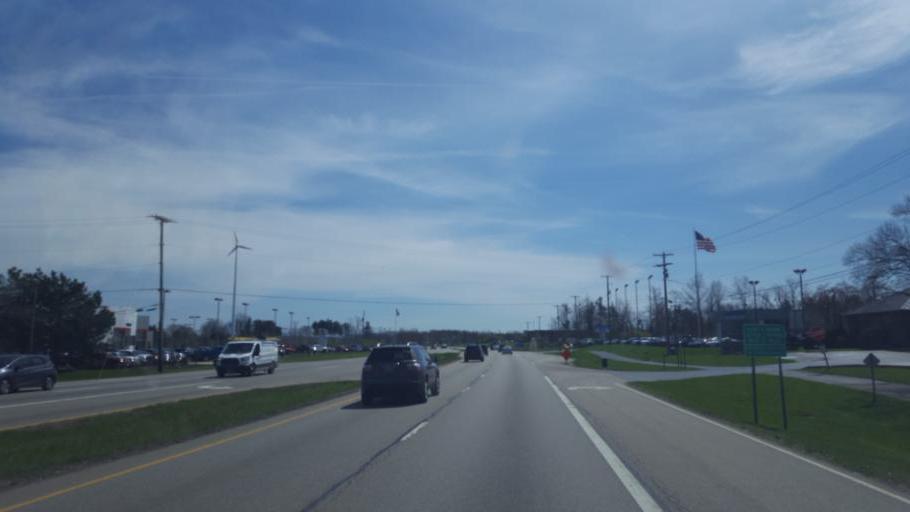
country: US
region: Ohio
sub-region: Delaware County
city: Delaware
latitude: 40.2717
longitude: -83.0710
